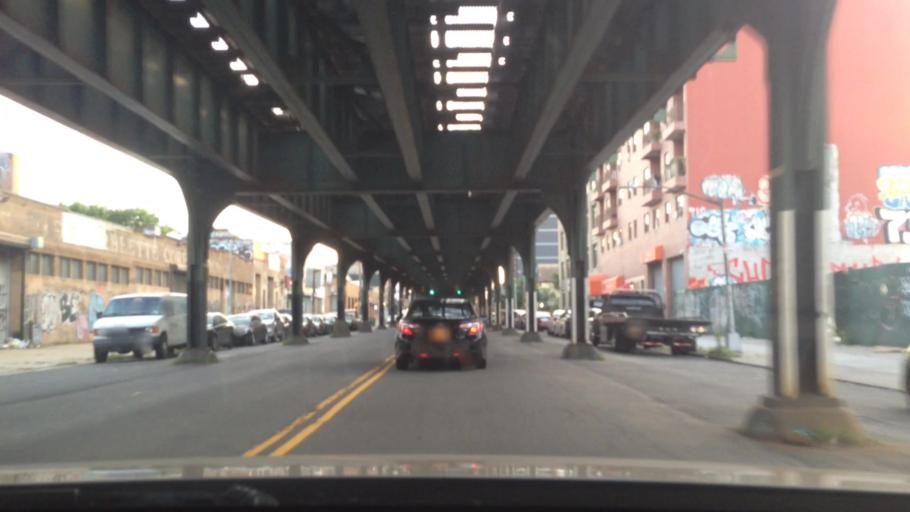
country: US
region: New York
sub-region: Queens County
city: Long Island City
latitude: 40.7539
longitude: -73.9320
